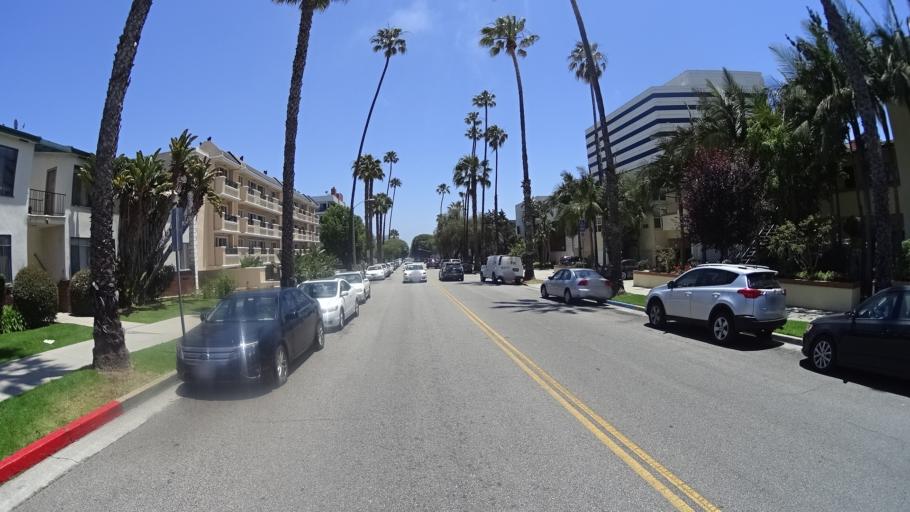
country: US
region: California
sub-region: Los Angeles County
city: Santa Monica
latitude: 34.0211
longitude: -118.4988
